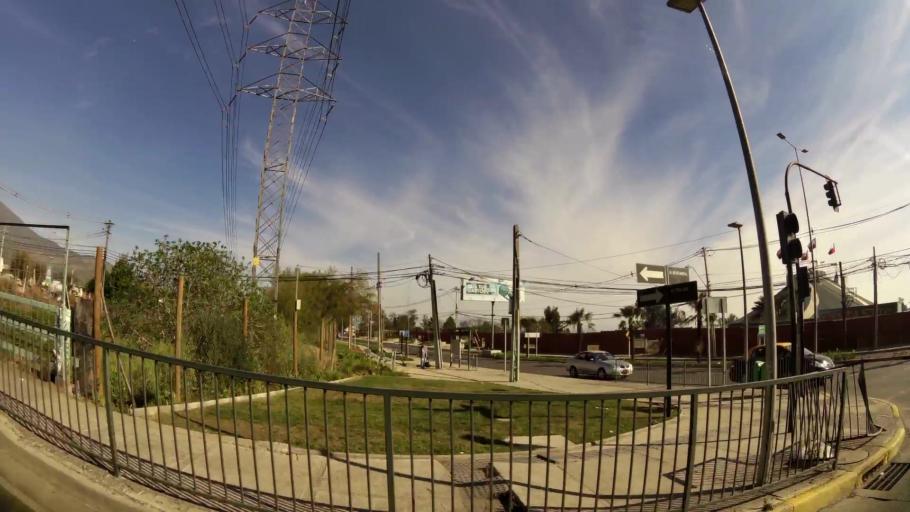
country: CL
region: Santiago Metropolitan
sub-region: Provincia de Santiago
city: Villa Presidente Frei, Nunoa, Santiago, Chile
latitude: -33.5118
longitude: -70.5604
